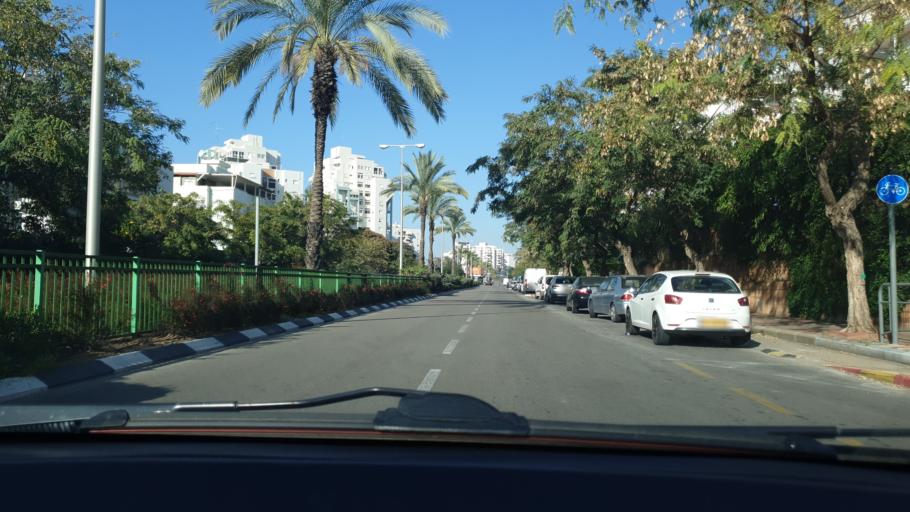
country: IL
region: Central District
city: Rishon LeZiyyon
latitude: 31.9754
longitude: 34.7771
